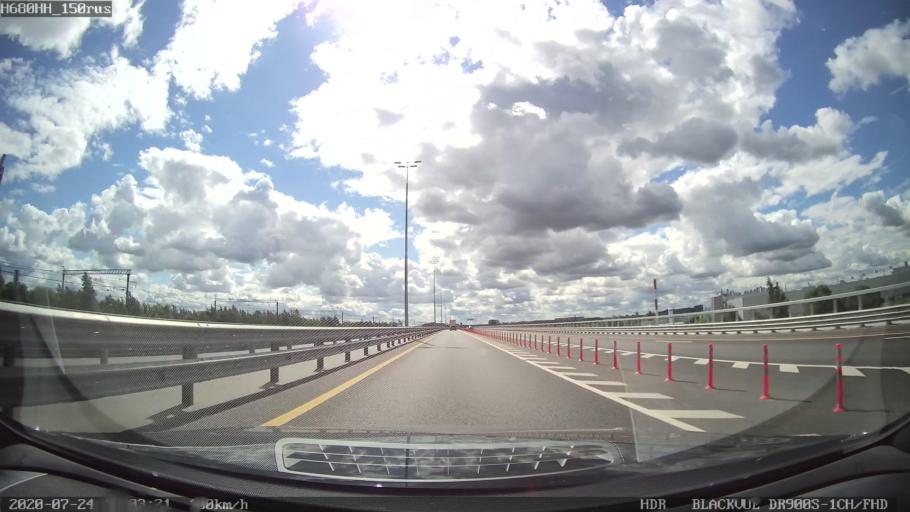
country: RU
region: St.-Petersburg
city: Shushary
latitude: 59.8039
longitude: 30.3358
